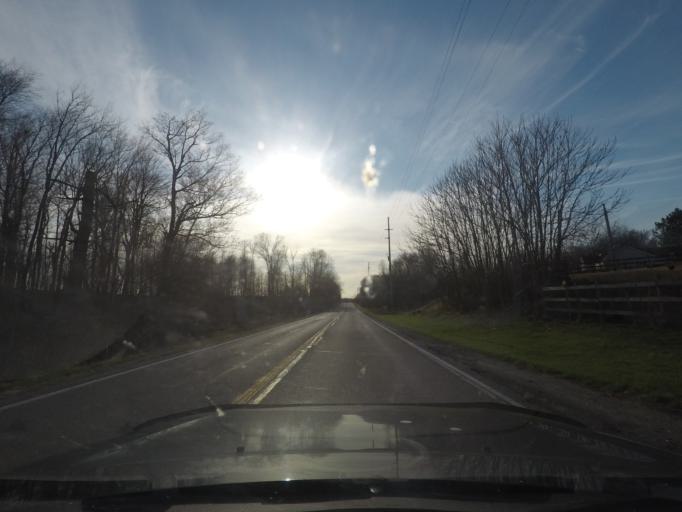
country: US
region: Indiana
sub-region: Saint Joseph County
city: Walkerton
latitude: 41.4481
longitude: -86.4164
